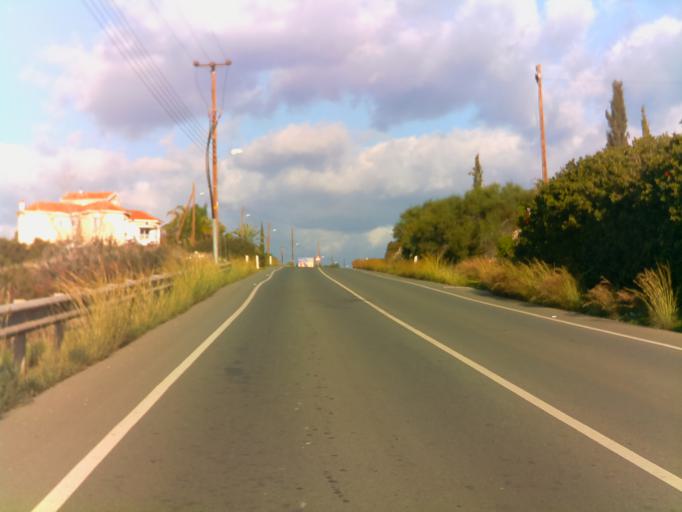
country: CY
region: Pafos
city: Pegeia
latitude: 34.8713
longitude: 32.3614
